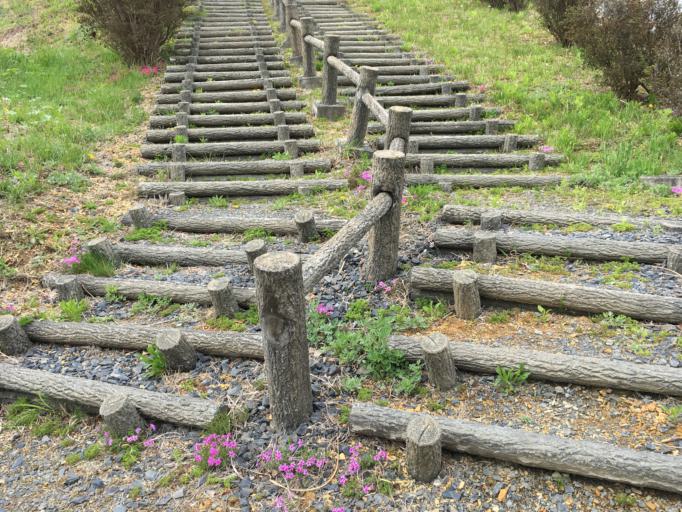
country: JP
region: Iwate
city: Ichinoseki
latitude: 38.7950
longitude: 141.4051
